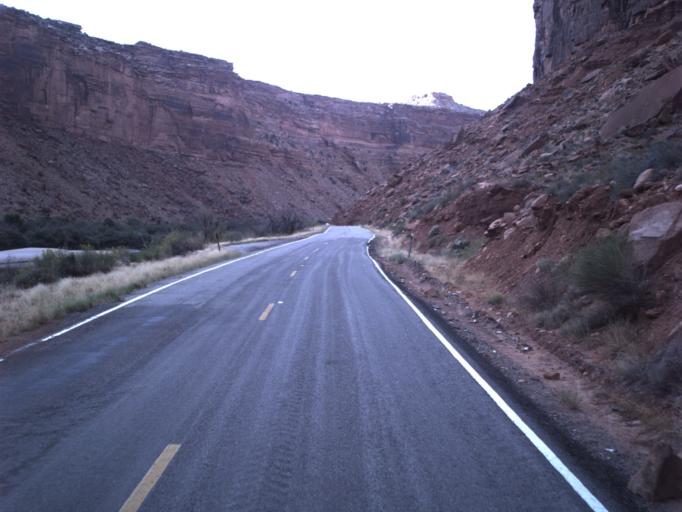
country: US
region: Utah
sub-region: Grand County
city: Moab
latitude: 38.7909
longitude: -109.3354
